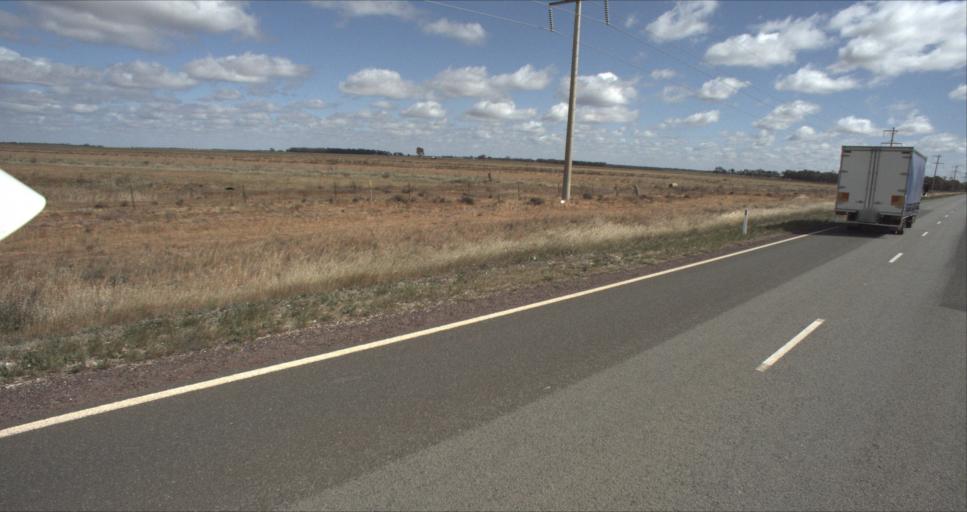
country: AU
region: New South Wales
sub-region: Murrumbidgee Shire
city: Darlington Point
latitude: -34.5835
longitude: 146.1647
